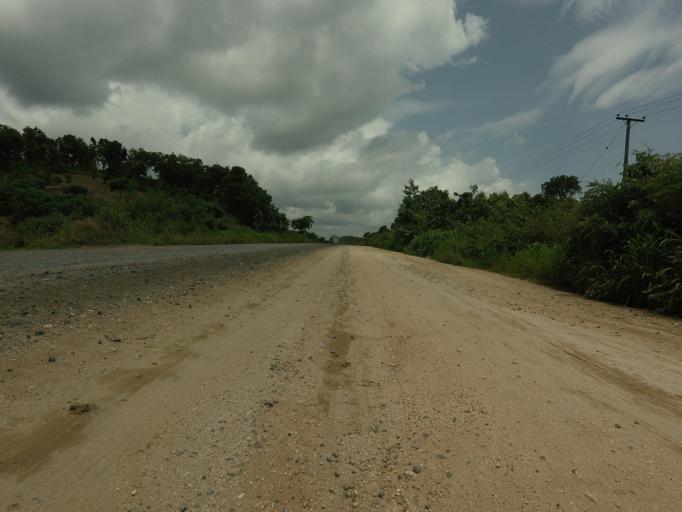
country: GH
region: Volta
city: Ho
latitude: 6.6734
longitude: 0.3119
